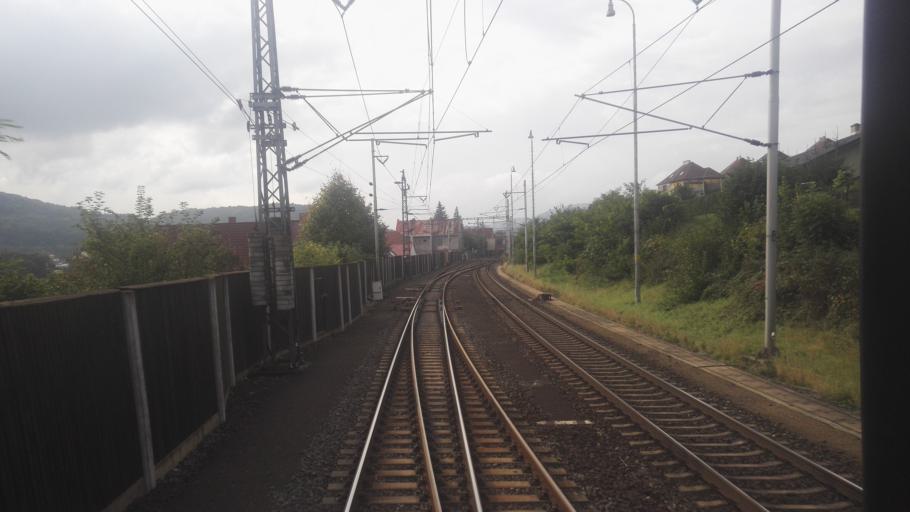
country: CZ
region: Ustecky
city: Velke Brezno
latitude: 50.6689
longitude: 14.1470
